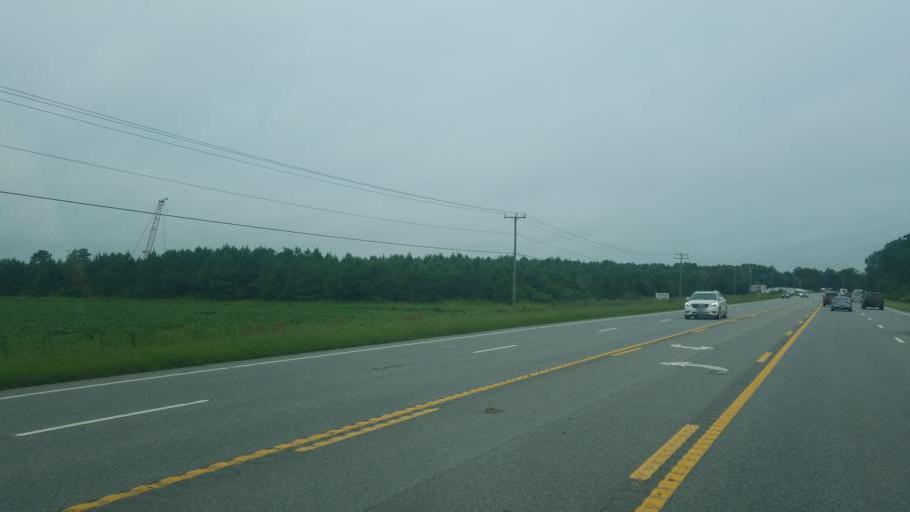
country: US
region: North Carolina
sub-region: Currituck County
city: Moyock
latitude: 36.4762
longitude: -76.1238
